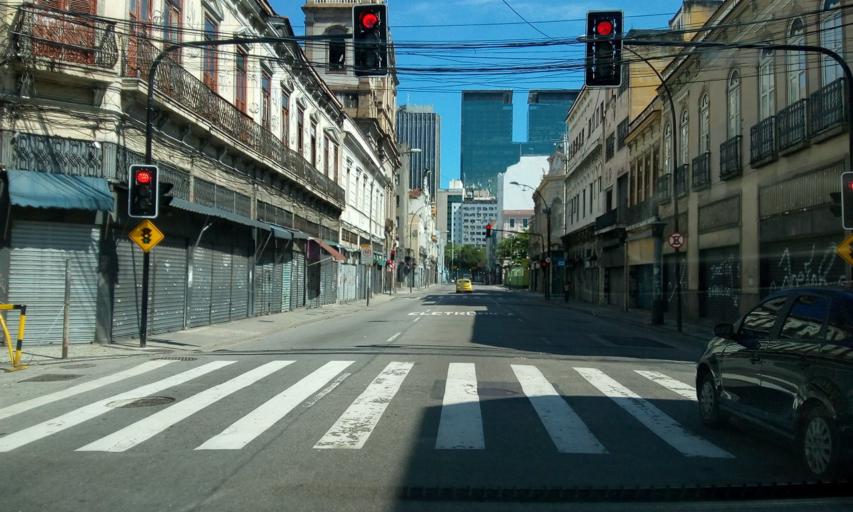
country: BR
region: Rio de Janeiro
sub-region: Rio De Janeiro
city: Rio de Janeiro
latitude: -22.9038
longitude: -43.1834
